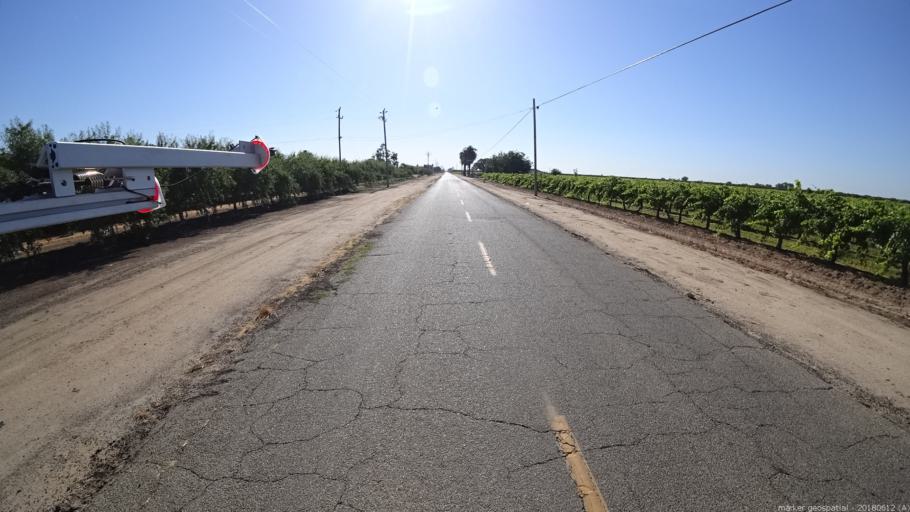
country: US
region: California
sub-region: Madera County
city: Fairmead
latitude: 37.0110
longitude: -120.1544
